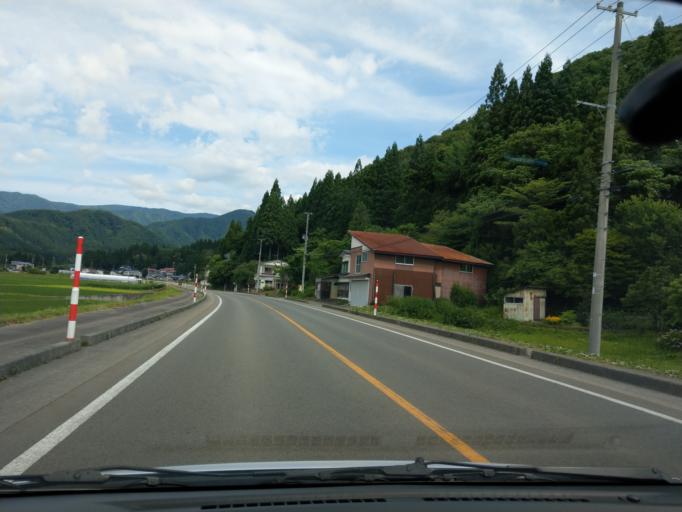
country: JP
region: Akita
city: Kakunodatemachi
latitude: 39.6795
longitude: 140.5630
